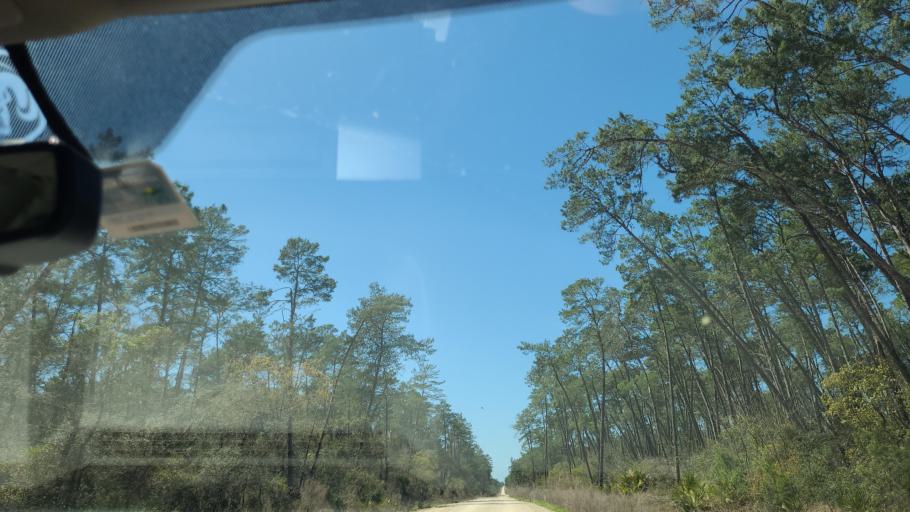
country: US
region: Florida
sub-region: Putnam County
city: Interlachen
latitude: 29.4283
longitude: -81.8845
